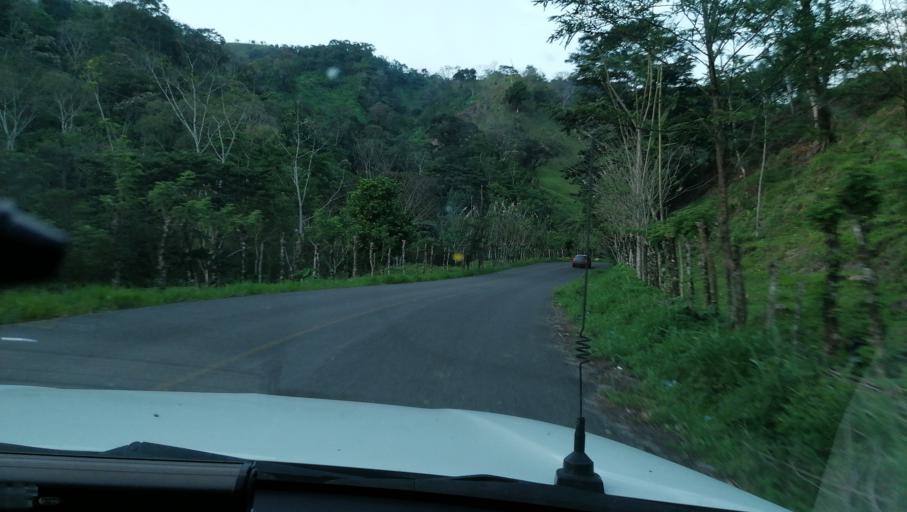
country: MX
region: Chiapas
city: Ostuacan
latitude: 17.4171
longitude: -93.3417
